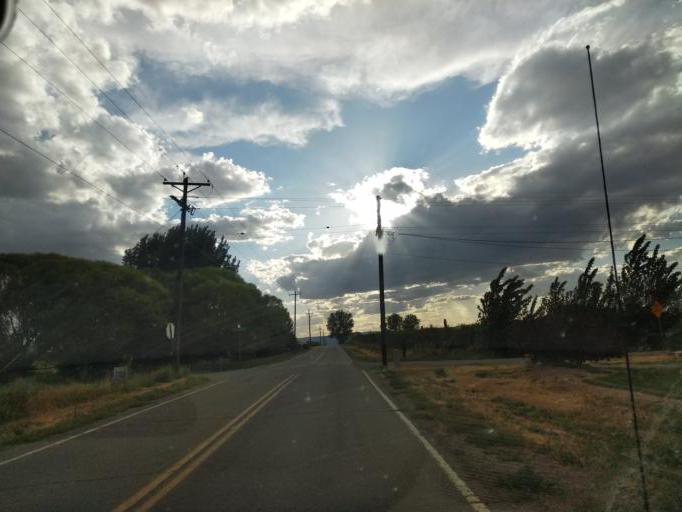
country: US
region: Colorado
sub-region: Mesa County
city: Clifton
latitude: 39.0559
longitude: -108.4312
